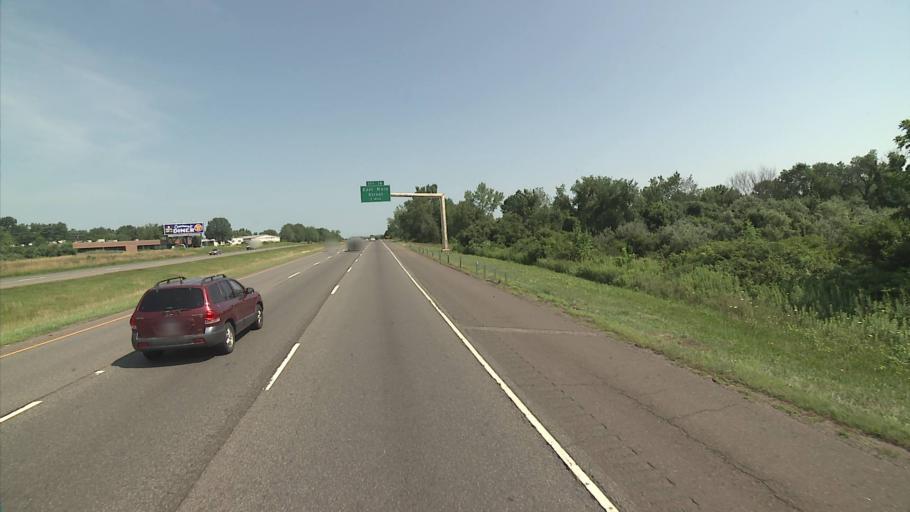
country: US
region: Connecticut
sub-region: New Haven County
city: Meriden
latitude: 41.5053
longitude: -72.7691
